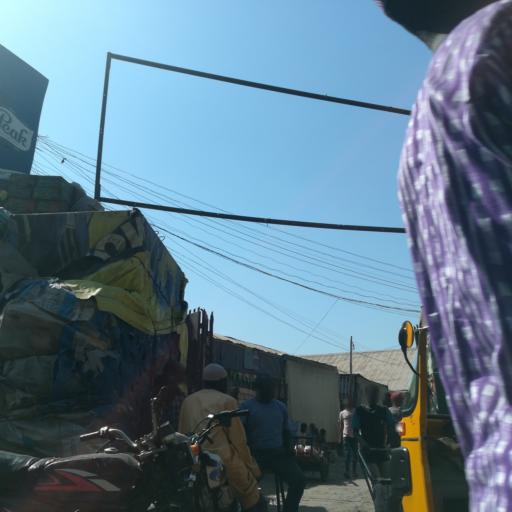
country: NG
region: Kano
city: Kano
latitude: 12.0102
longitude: 8.5378
